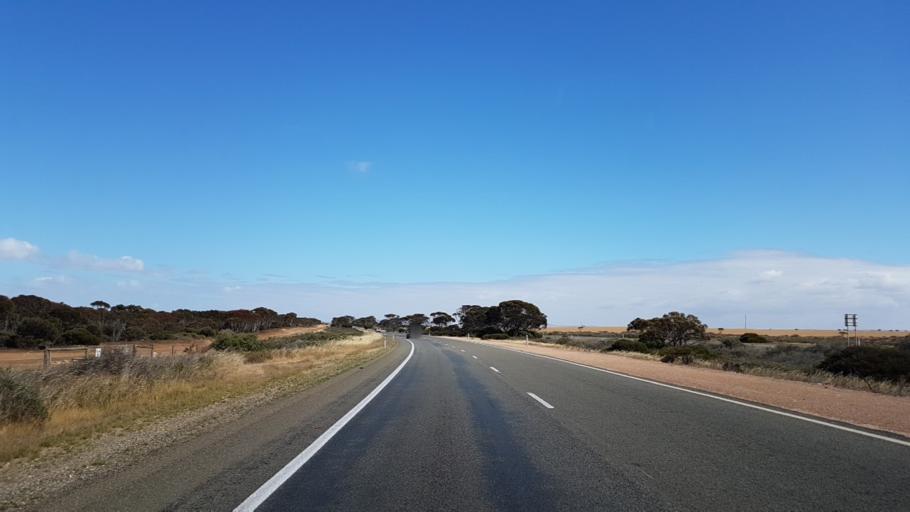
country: AU
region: South Australia
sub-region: Wakefield
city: Balaklava
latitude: -34.2548
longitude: 138.2219
